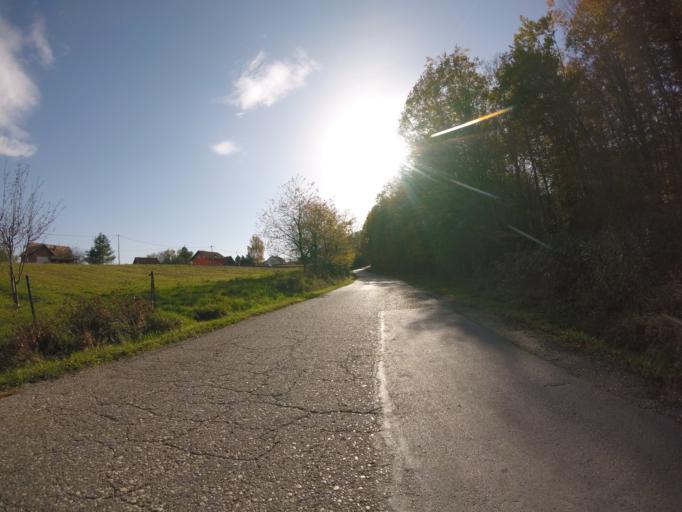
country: HR
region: Zagrebacka
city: Mraclin
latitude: 45.6092
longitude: 16.0670
